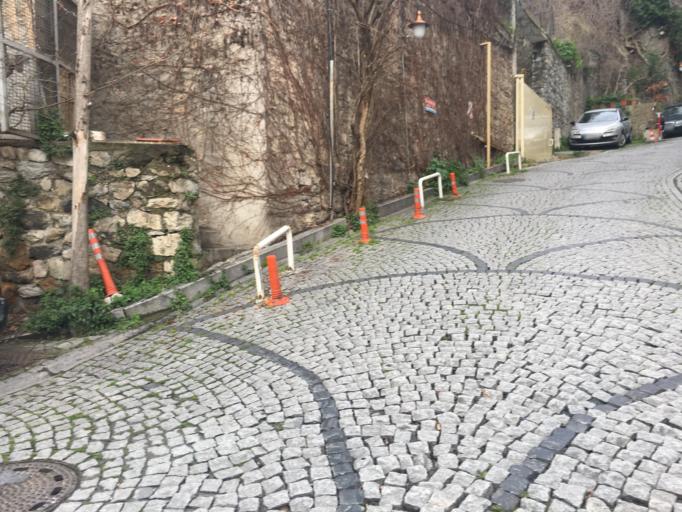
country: TR
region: Istanbul
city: UEskuedar
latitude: 41.0679
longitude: 29.0415
